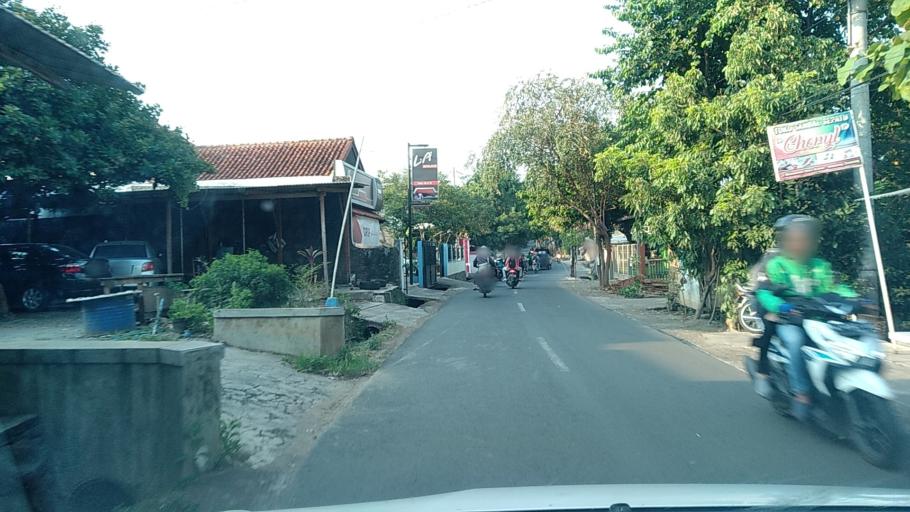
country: ID
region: Central Java
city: Semarang
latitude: -7.0672
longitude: 110.4398
